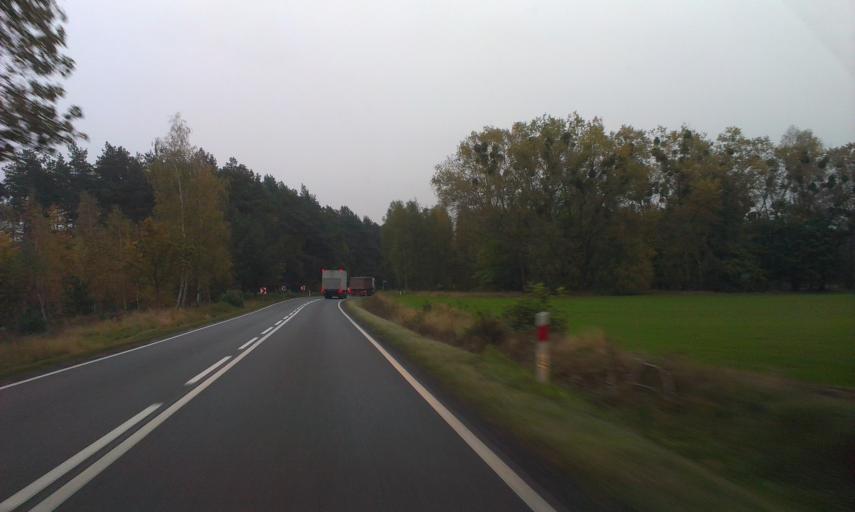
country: PL
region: Kujawsko-Pomorskie
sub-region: Powiat sepolenski
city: Sepolno Krajenskie
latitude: 53.4359
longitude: 17.5687
